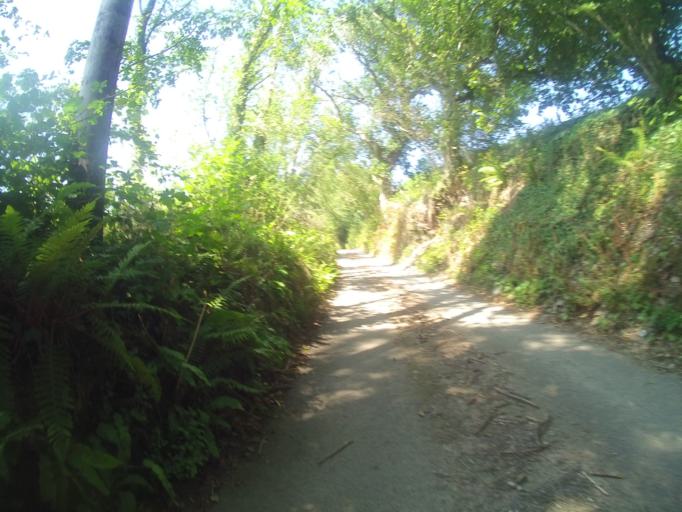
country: GB
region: England
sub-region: Devon
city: Dartmouth
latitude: 50.3594
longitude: -3.6181
